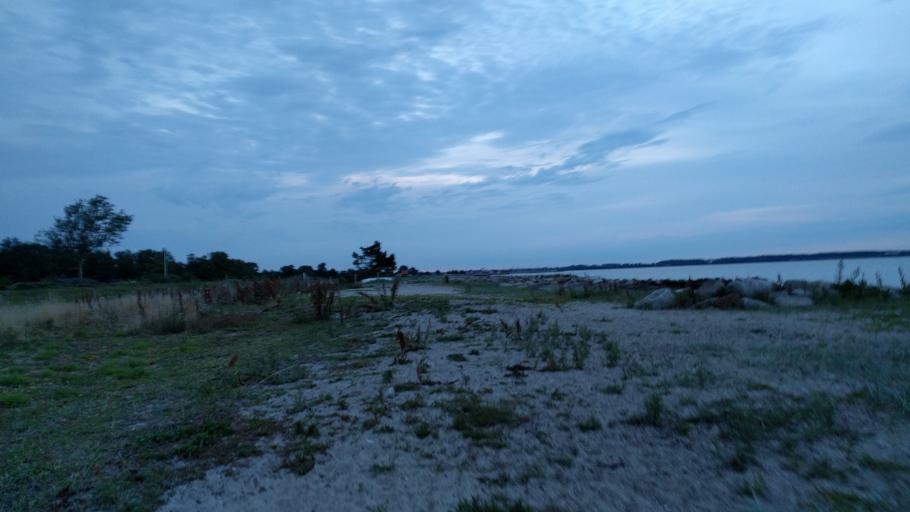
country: DK
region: Central Jutland
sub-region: Hedensted Kommune
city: Juelsminde
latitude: 55.7032
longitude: 10.0248
